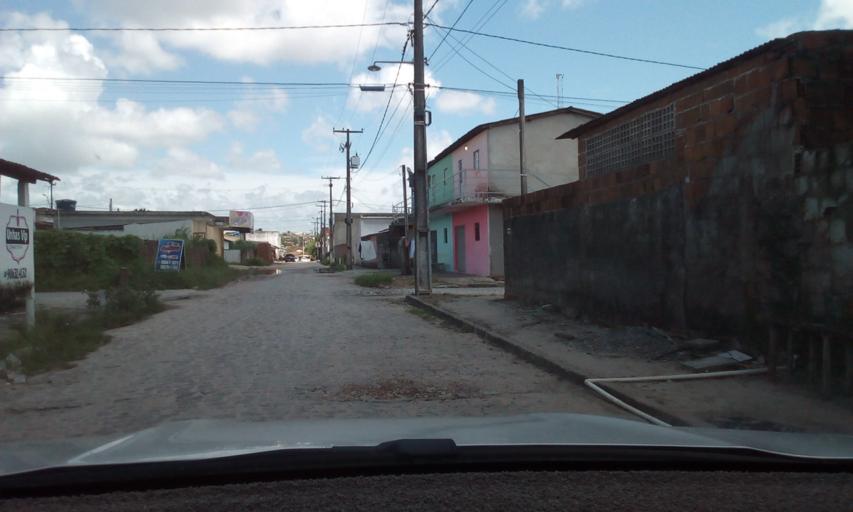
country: BR
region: Paraiba
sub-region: Bayeux
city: Bayeux
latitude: -7.1190
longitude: -34.9373
